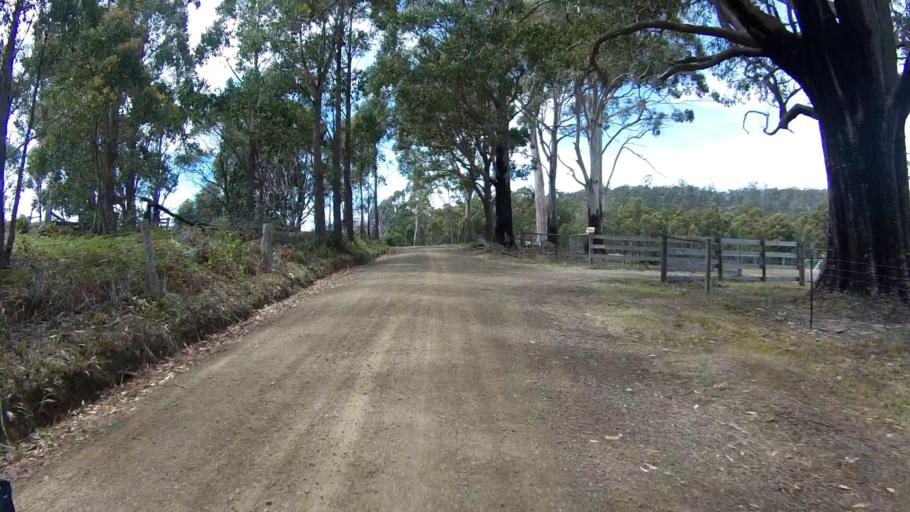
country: AU
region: Tasmania
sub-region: Sorell
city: Sorell
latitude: -42.7896
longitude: 147.7133
